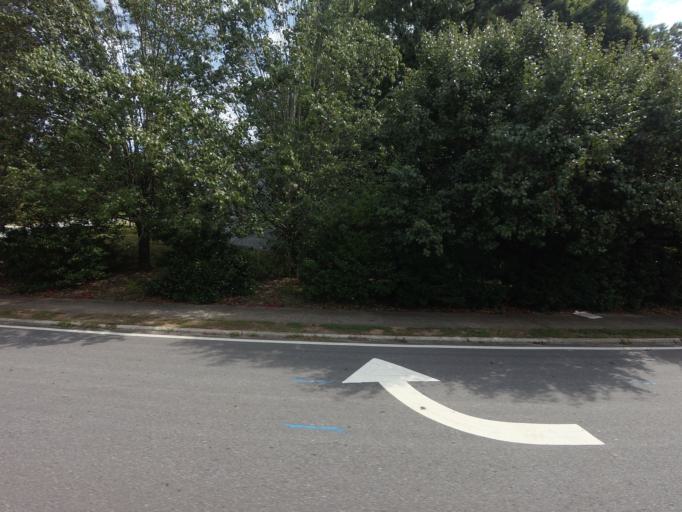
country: US
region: Georgia
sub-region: Fulton County
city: Johns Creek
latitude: 34.0513
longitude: -84.1844
